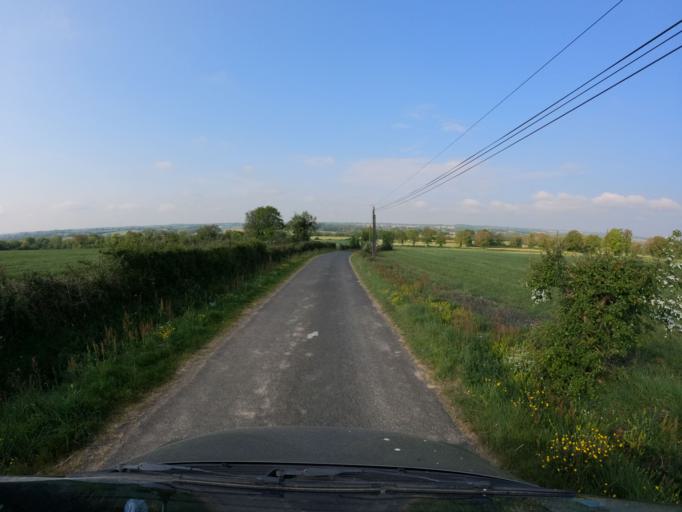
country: FR
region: Pays de la Loire
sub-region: Departement de Maine-et-Loire
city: Saint-Andre-de-la-Marche
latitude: 47.0738
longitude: -0.9959
